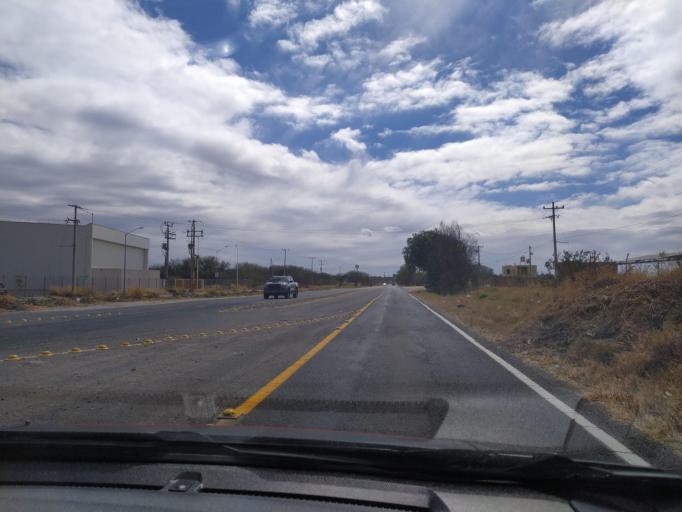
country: LA
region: Oudomxai
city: Muang La
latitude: 21.0037
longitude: 101.8313
